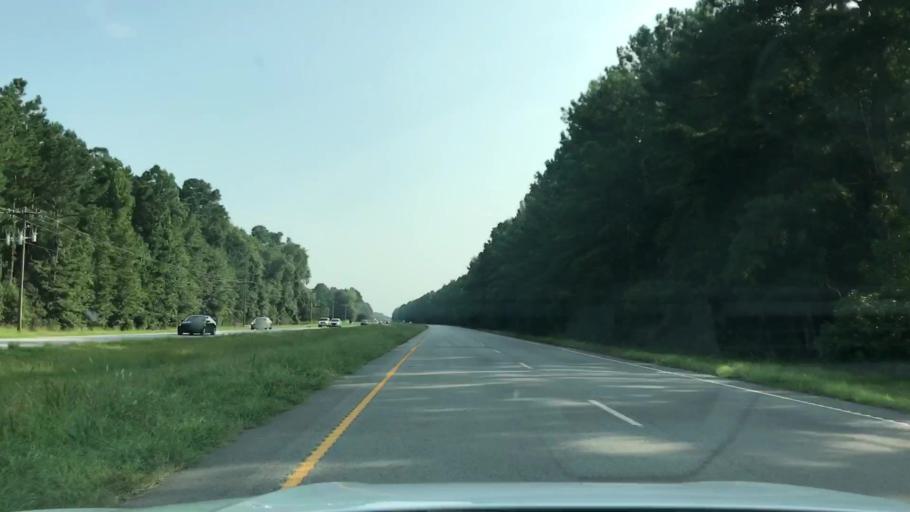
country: US
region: South Carolina
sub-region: Charleston County
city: Awendaw
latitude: 33.1212
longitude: -79.4524
